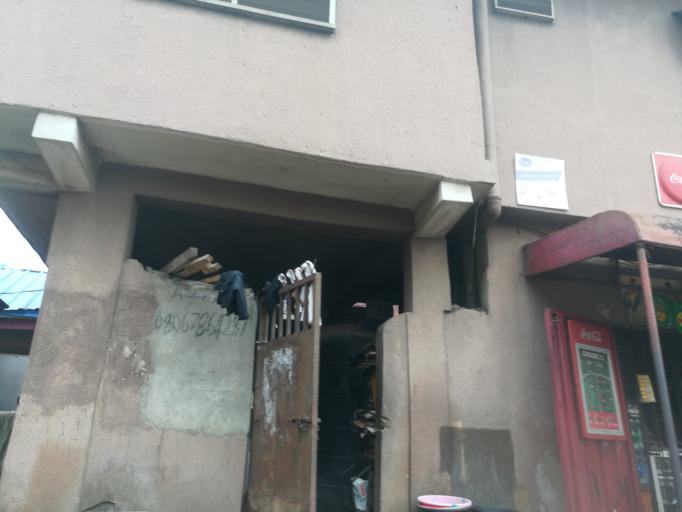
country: NG
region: Lagos
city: Ojota
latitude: 6.5715
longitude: 3.3637
